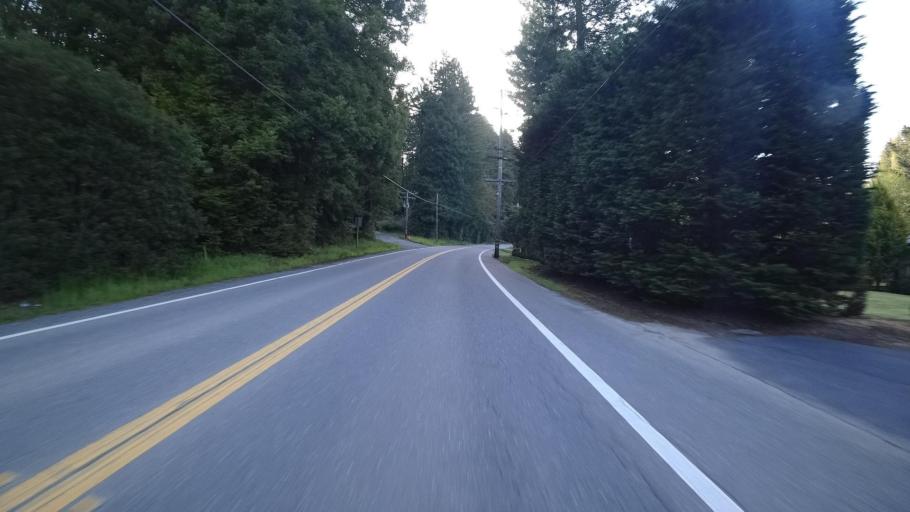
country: US
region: California
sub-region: Humboldt County
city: Myrtletown
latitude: 40.7598
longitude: -124.0550
